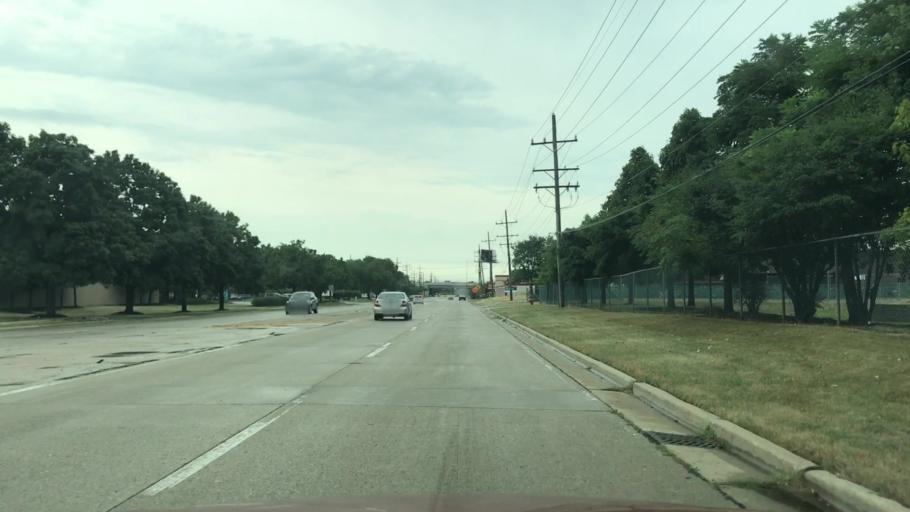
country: US
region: Illinois
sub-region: Cook County
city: Des Plaines
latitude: 42.0184
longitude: -87.9209
